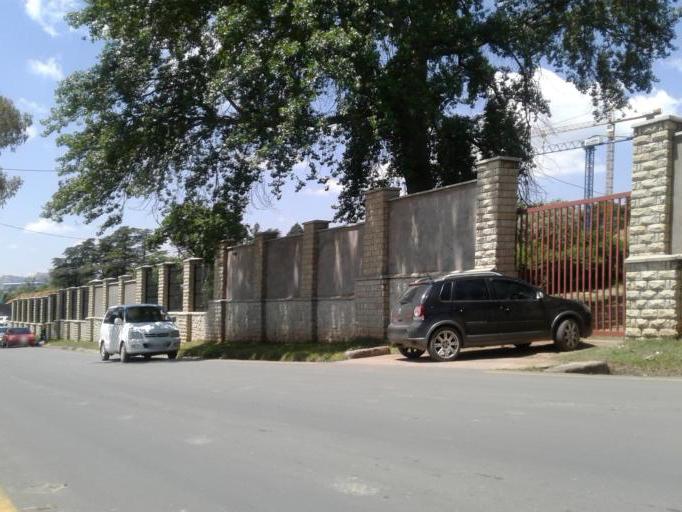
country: LS
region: Maseru
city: Maseru
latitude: -29.3098
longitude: 27.4843
